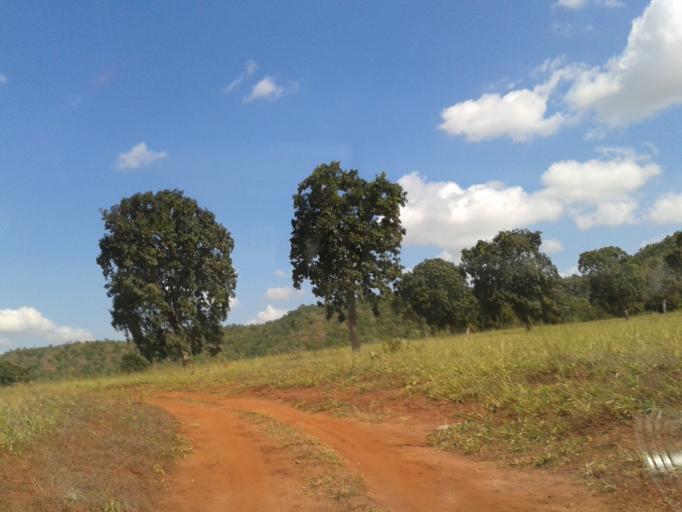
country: BR
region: Minas Gerais
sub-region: Santa Vitoria
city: Santa Vitoria
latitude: -19.2527
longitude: -50.0605
